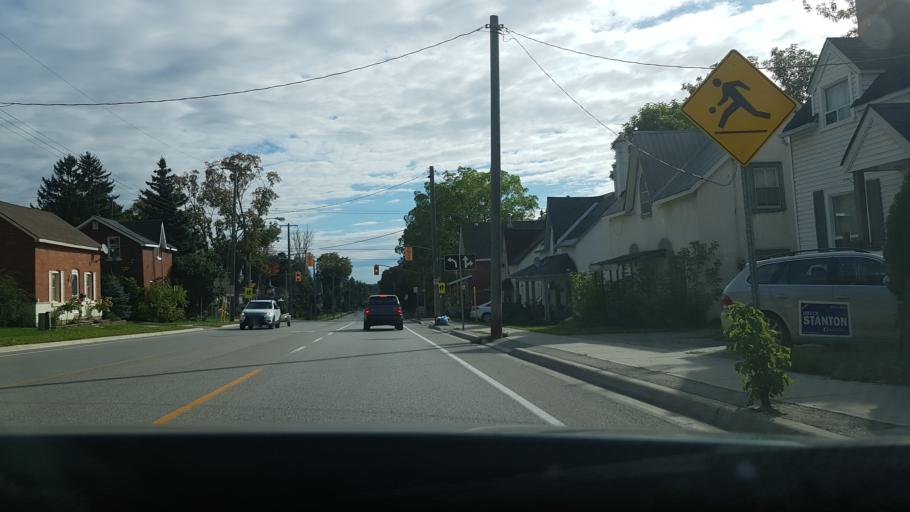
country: CA
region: Ontario
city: Orillia
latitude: 44.6093
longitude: -79.4270
